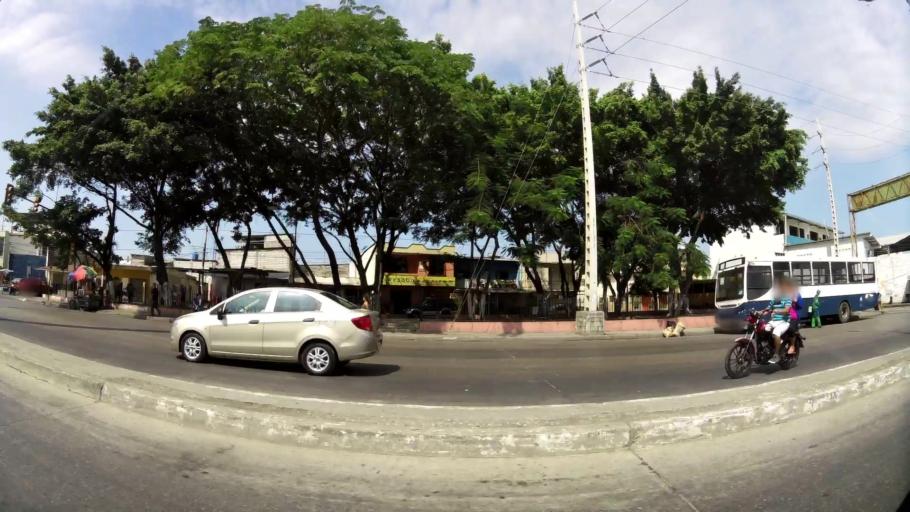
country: EC
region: Guayas
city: Guayaquil
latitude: -2.2610
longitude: -79.8791
